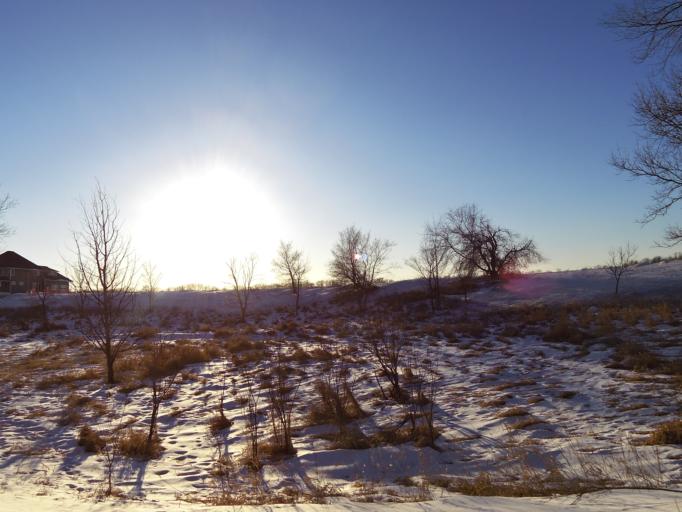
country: US
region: Minnesota
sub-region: Washington County
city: Lake Elmo
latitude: 44.9897
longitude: -92.8431
